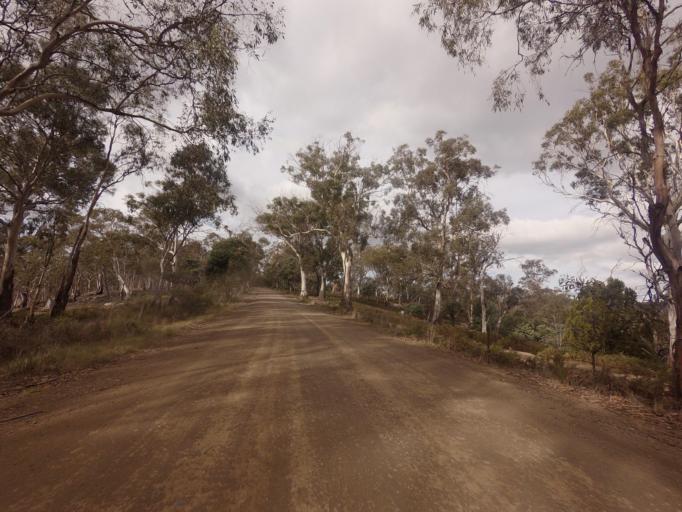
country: AU
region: Tasmania
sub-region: Brighton
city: Bridgewater
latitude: -42.4598
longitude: 147.2566
